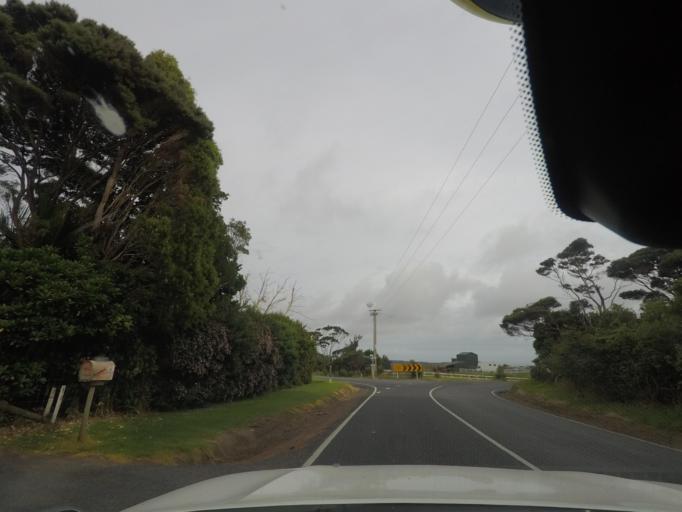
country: NZ
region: Auckland
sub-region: Auckland
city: Parakai
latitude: -36.4868
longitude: 174.2471
